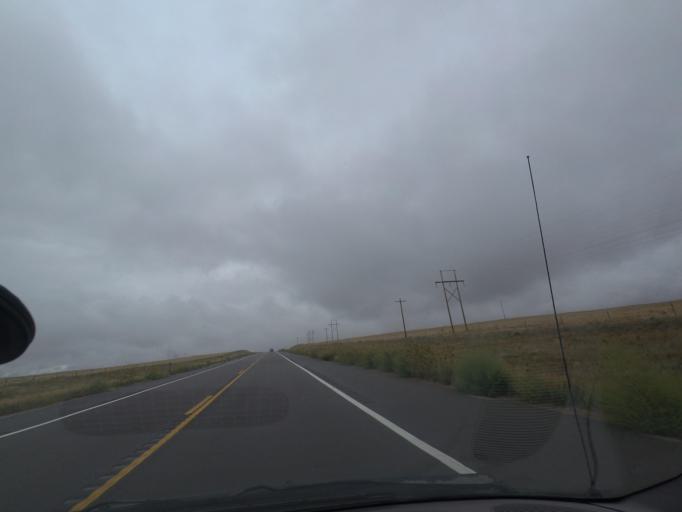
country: US
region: Colorado
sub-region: Lincoln County
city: Limon
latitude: 39.7400
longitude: -103.6100
